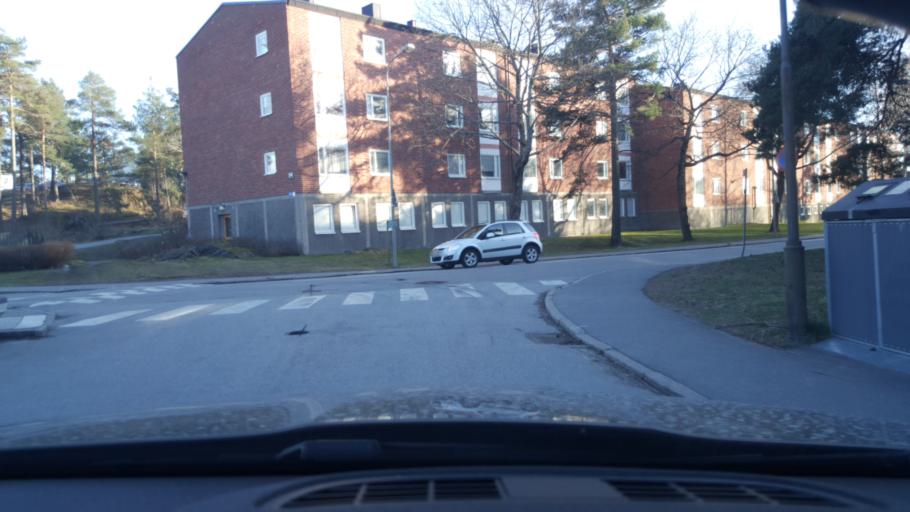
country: SE
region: Stockholm
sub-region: Stockholms Kommun
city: Arsta
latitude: 59.2637
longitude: 18.0512
